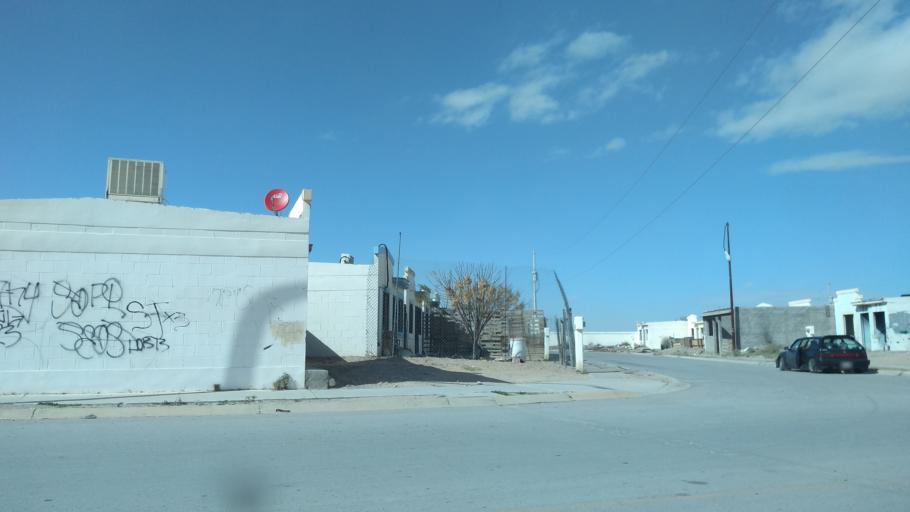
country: US
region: Texas
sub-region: El Paso County
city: San Elizario
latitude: 31.5713
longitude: -106.3300
